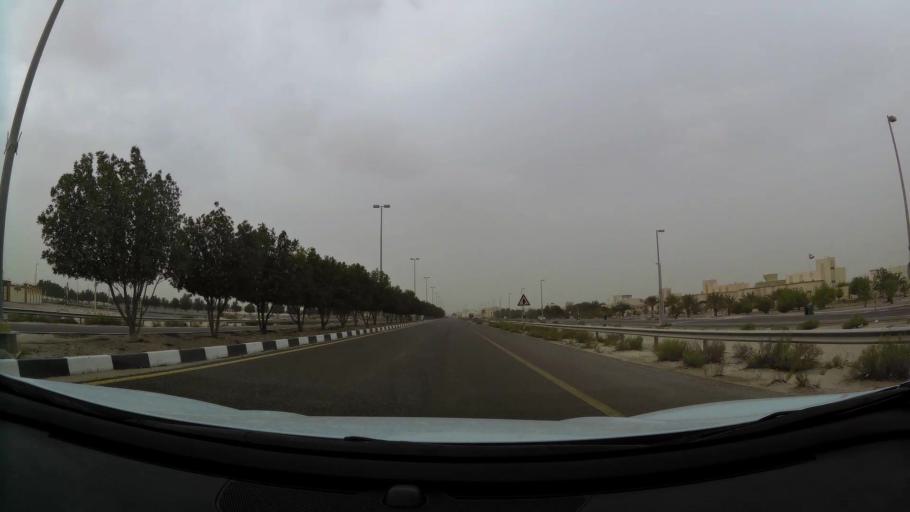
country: AE
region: Abu Dhabi
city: Abu Dhabi
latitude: 24.3907
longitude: 54.7093
